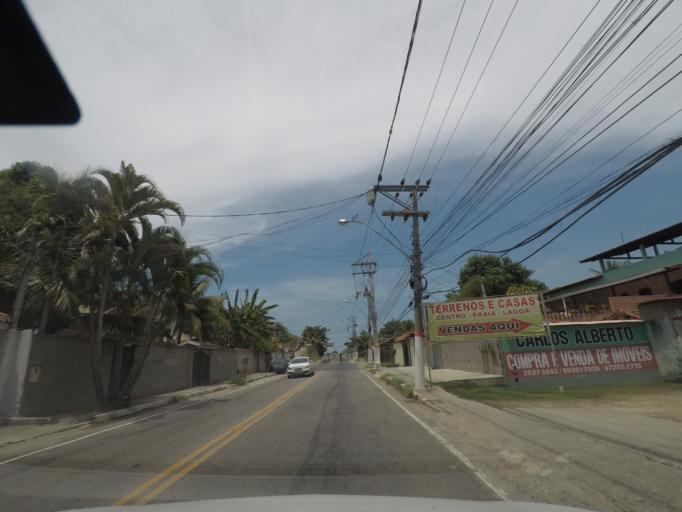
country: BR
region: Rio de Janeiro
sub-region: Marica
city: Marica
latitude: -22.9372
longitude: -42.8286
